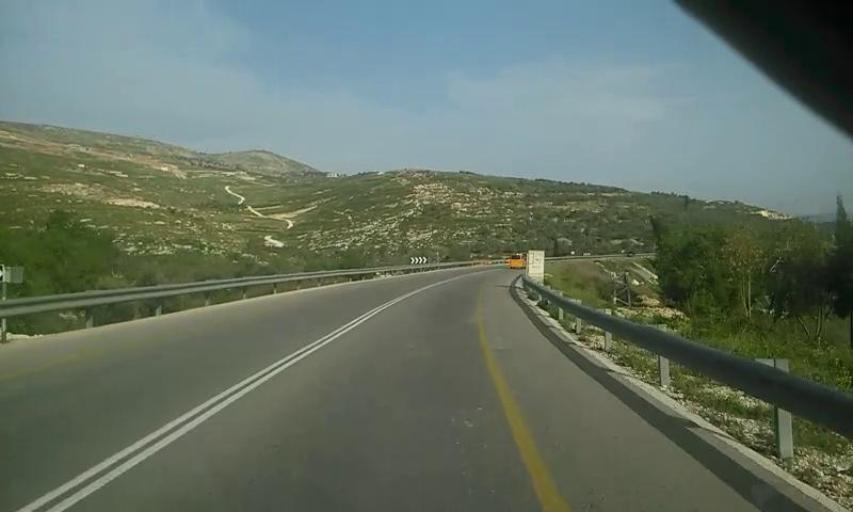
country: PS
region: West Bank
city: Madama
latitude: 32.1890
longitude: 35.2296
